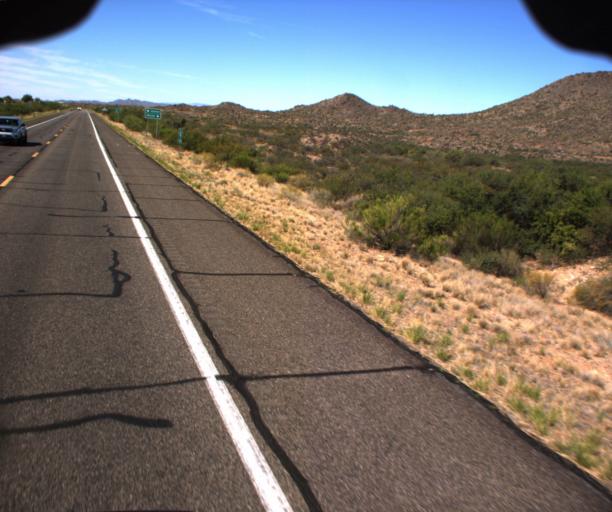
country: US
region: Arizona
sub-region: Yavapai County
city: Congress
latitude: 34.1850
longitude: -112.8233
